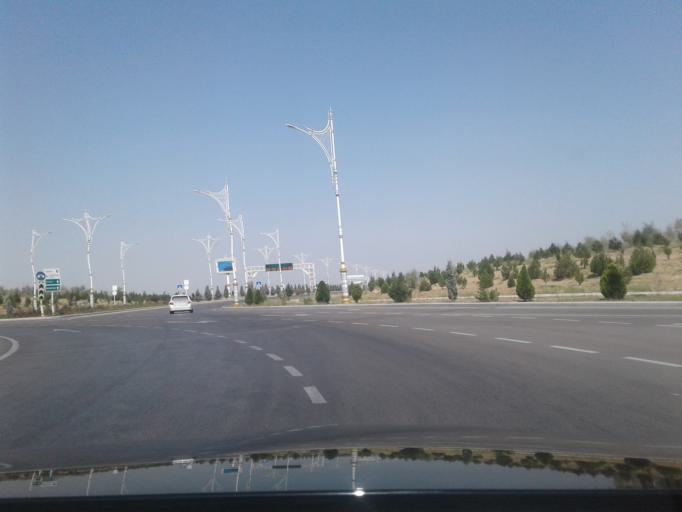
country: TM
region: Ahal
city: Ashgabat
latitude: 37.8777
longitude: 58.4227
